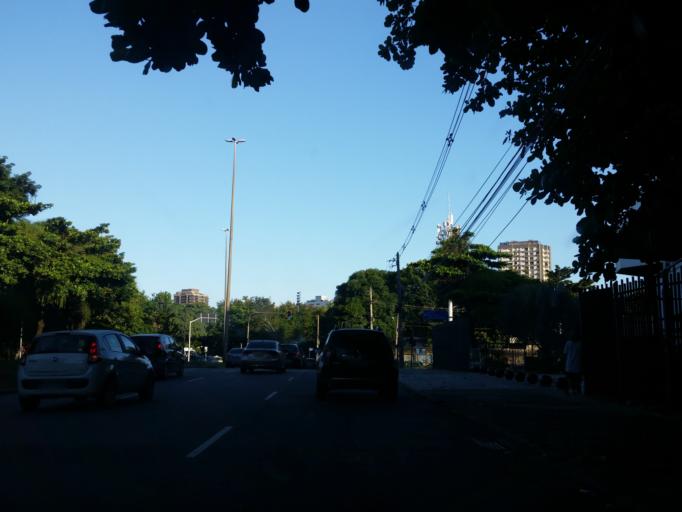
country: BR
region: Rio de Janeiro
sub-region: Rio De Janeiro
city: Rio de Janeiro
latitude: -22.9781
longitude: -43.2185
